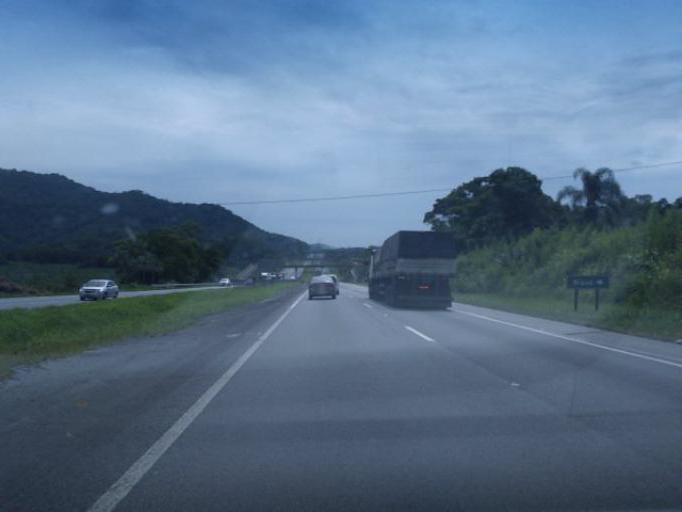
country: BR
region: Sao Paulo
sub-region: Miracatu
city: Miracatu
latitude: -24.3104
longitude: -47.5103
